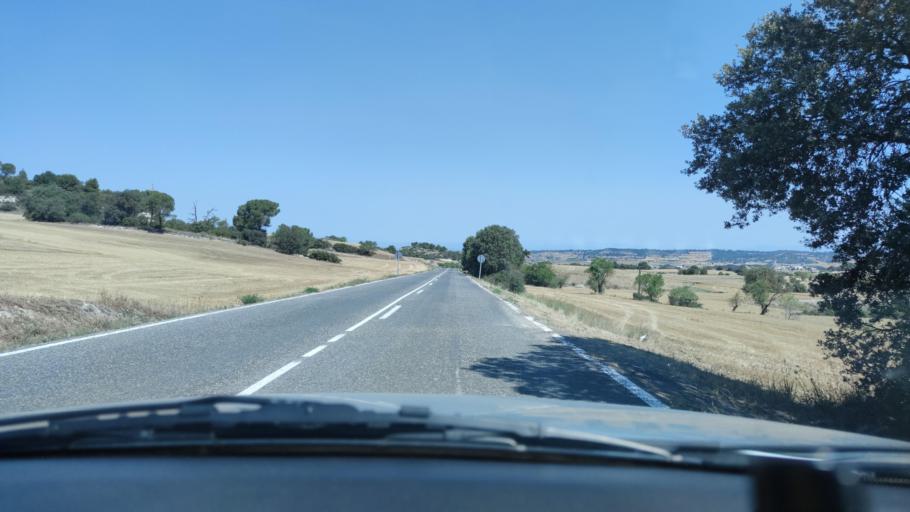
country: ES
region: Catalonia
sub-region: Provincia de Tarragona
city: Santa Coloma de Queralt
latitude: 41.6040
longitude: 1.3473
